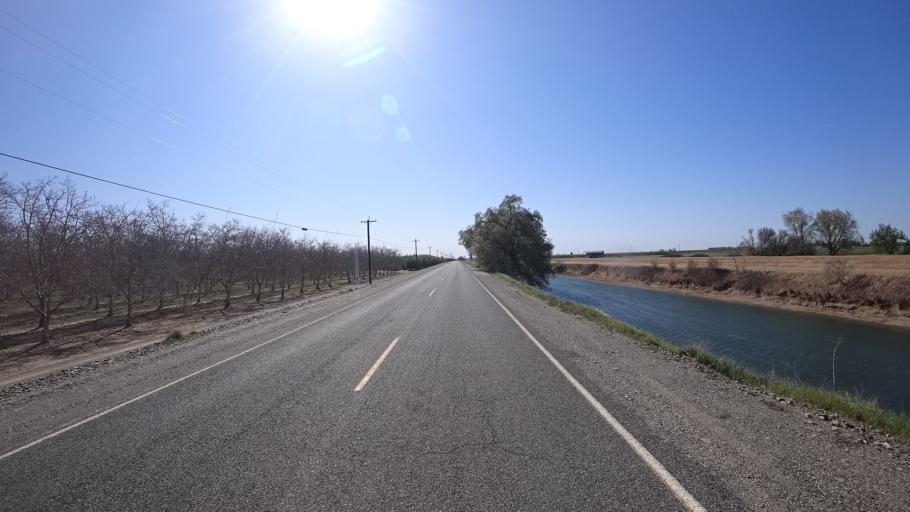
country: US
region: California
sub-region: Glenn County
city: Hamilton City
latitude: 39.7809
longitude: -122.0431
